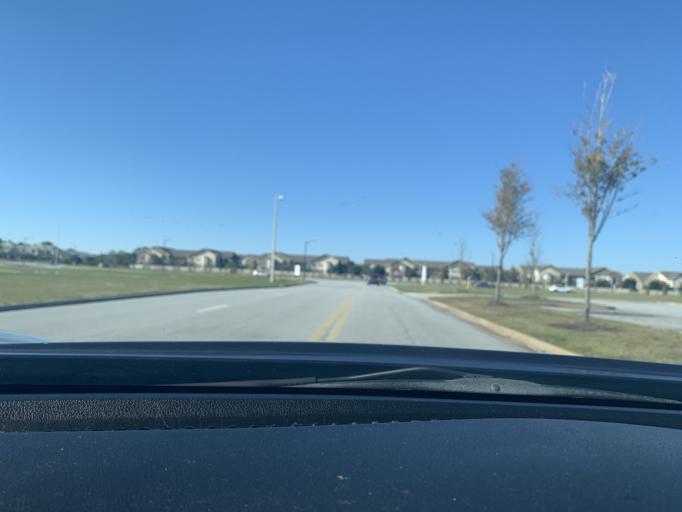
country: US
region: Georgia
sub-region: Chatham County
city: Pooler
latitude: 32.1326
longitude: -81.2458
